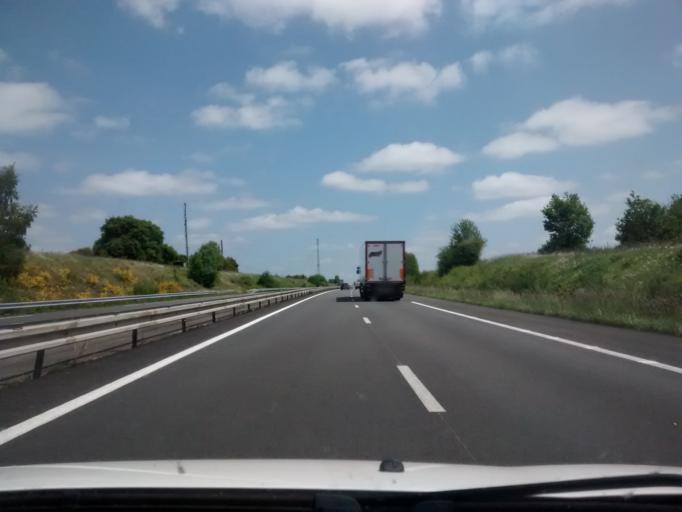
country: FR
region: Pays de la Loire
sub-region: Departement de la Mayenne
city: Vaiges
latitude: 48.0524
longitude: -0.4246
